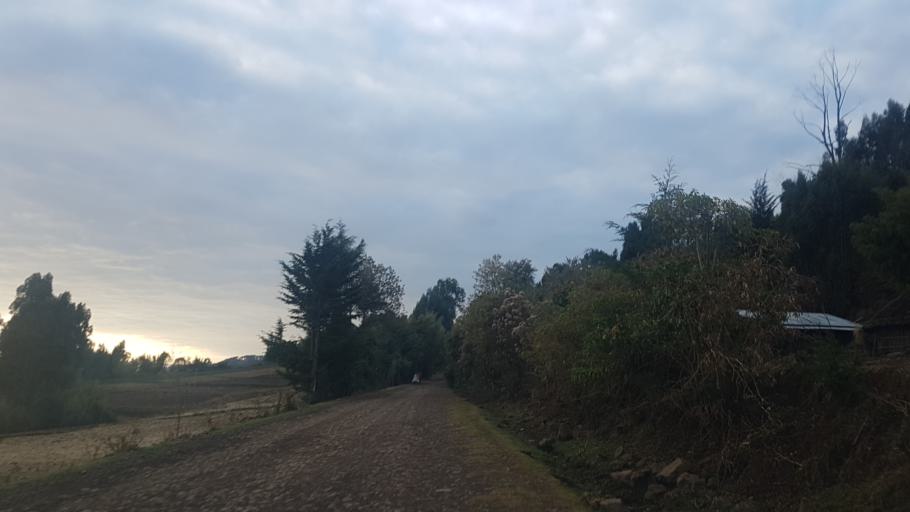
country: ET
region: Amhara
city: Finote Selam
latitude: 10.8056
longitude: 37.6589
